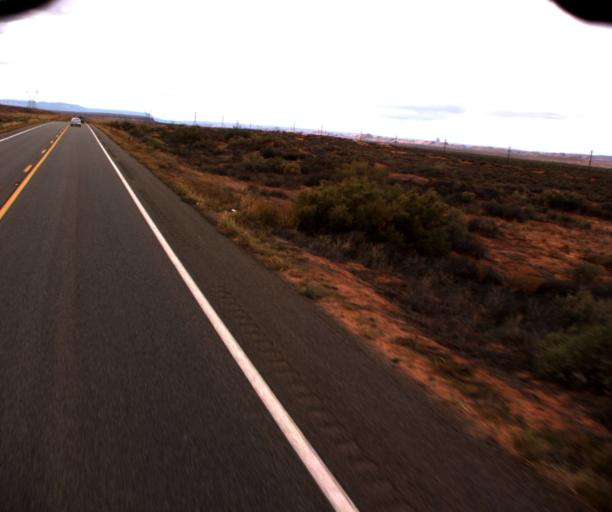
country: US
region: Arizona
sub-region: Navajo County
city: Kayenta
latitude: 36.8037
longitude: -109.9174
